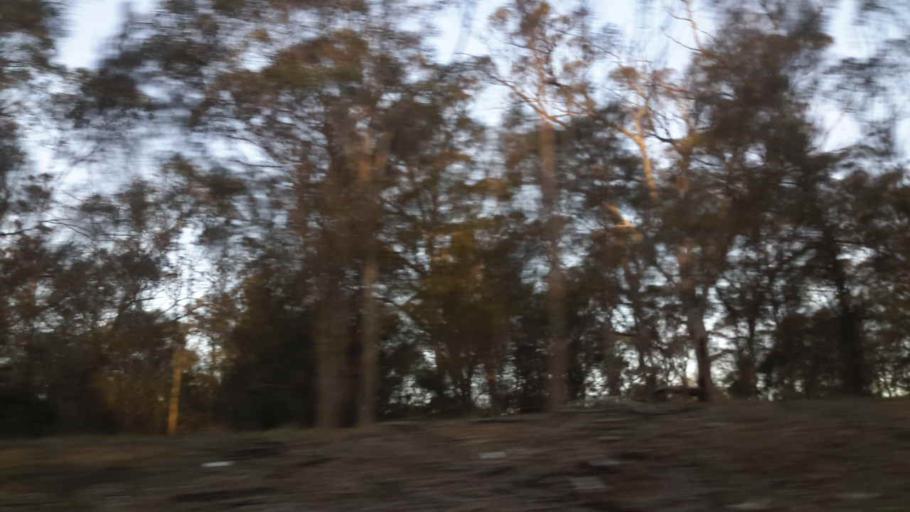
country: AU
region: New South Wales
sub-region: Wollondilly
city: Douglas Park
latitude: -34.2514
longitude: 150.7045
